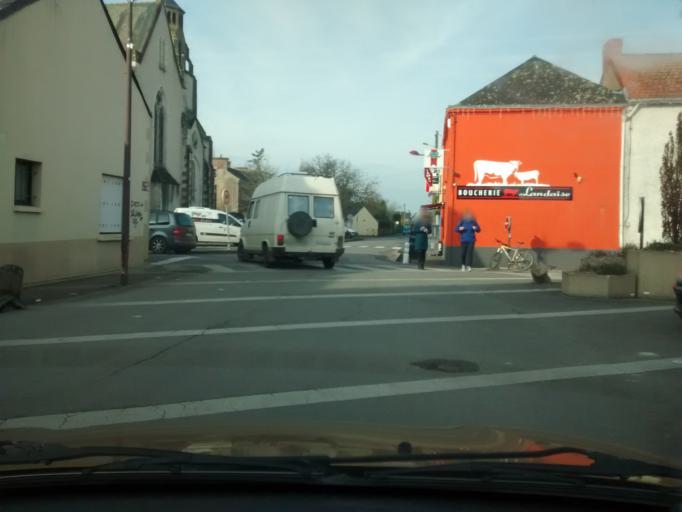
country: FR
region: Pays de la Loire
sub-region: Departement de la Loire-Atlantique
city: Notre-Dame-des-Landes
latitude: 47.3818
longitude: -1.7103
